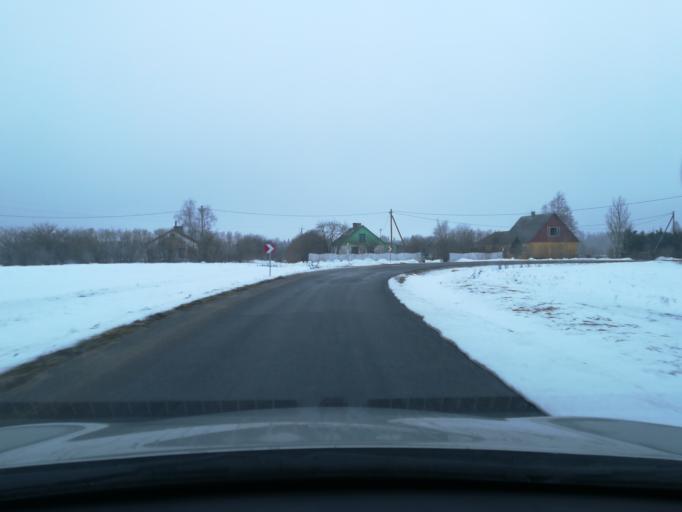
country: EE
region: Harju
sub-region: Raasiku vald
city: Raasiku
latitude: 59.3378
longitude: 25.2389
